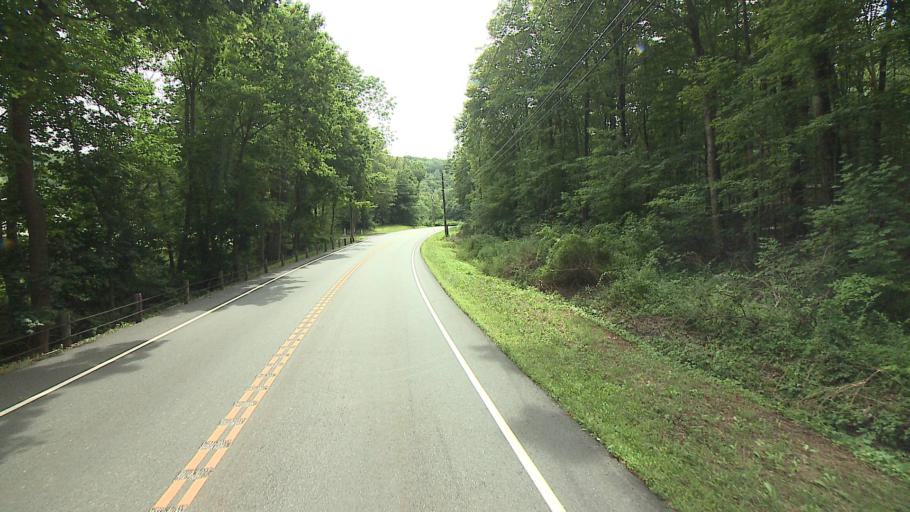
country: US
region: Connecticut
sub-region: Litchfield County
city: New Preston
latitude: 41.7084
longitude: -73.2974
